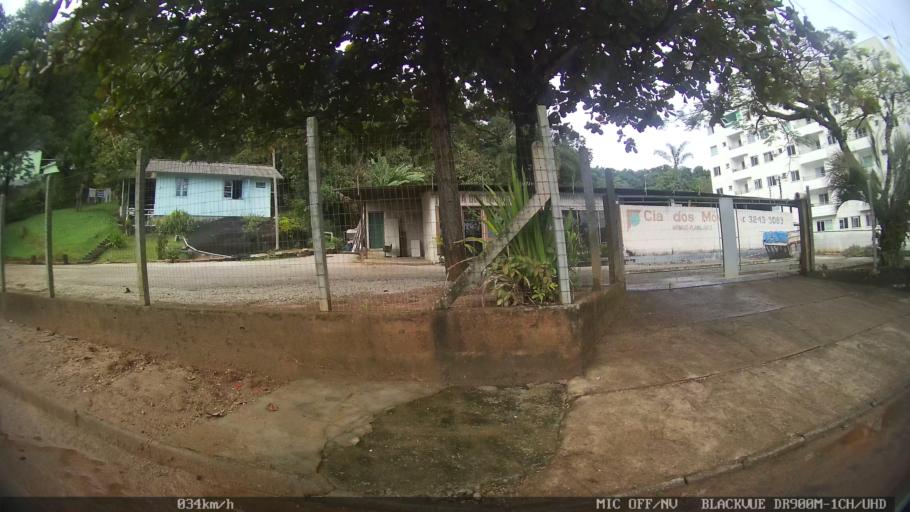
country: BR
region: Santa Catarina
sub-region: Biguacu
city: Biguacu
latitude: -27.5163
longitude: -48.6432
